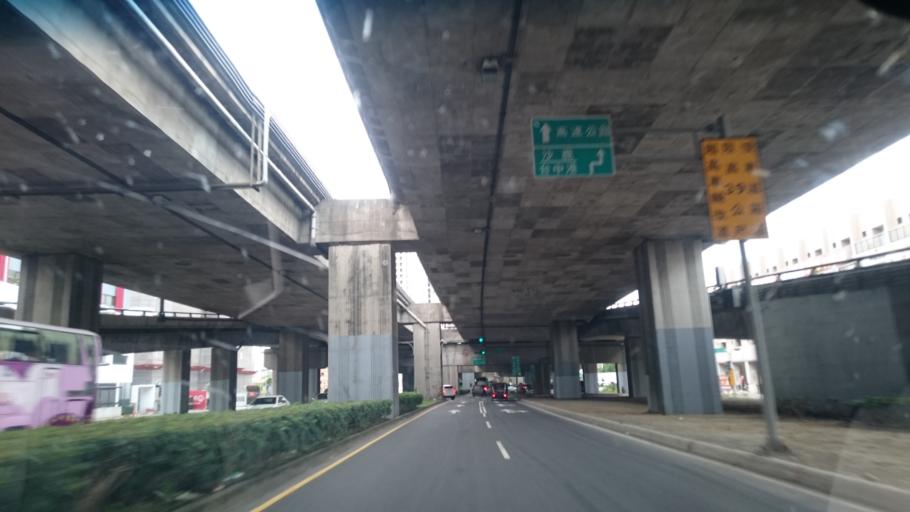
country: TW
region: Taiwan
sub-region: Taichung City
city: Taichung
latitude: 24.1751
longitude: 120.6340
